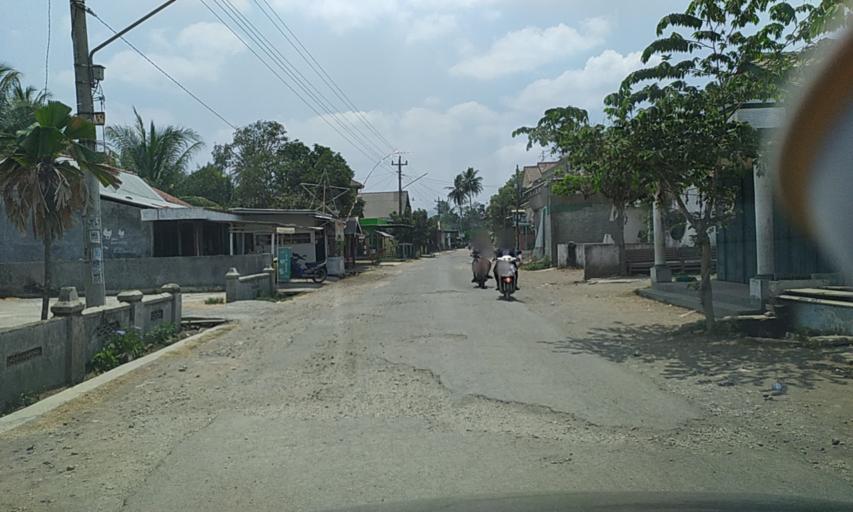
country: ID
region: Central Java
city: Sidakaya
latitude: -7.5642
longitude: 108.9168
